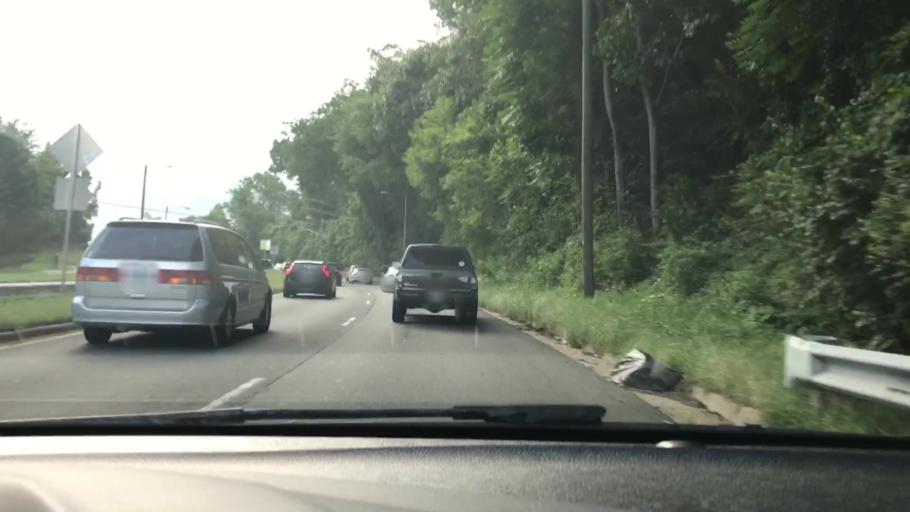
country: US
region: Virginia
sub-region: Fairfax County
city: Lake Barcroft
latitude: 38.8426
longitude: -77.1456
